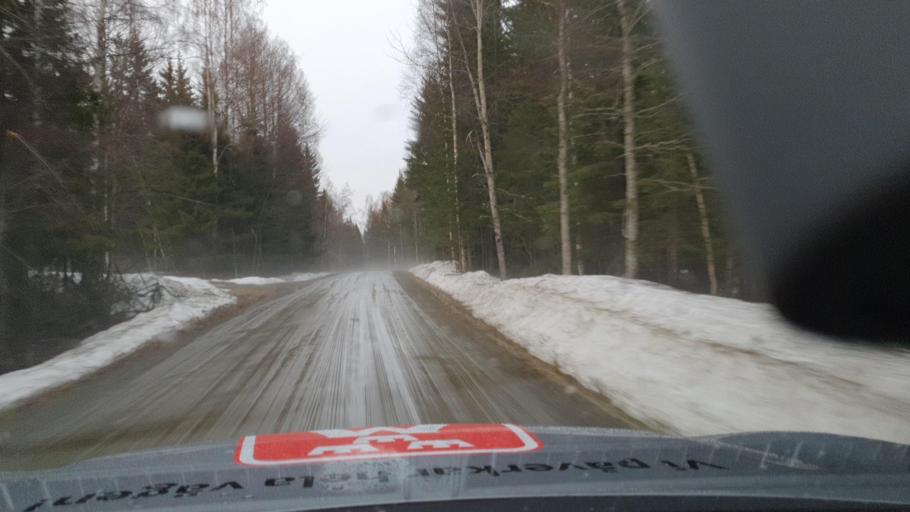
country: SE
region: Vaesternorrland
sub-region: OErnskoeldsviks Kommun
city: Bjasta
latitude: 63.2175
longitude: 18.2778
